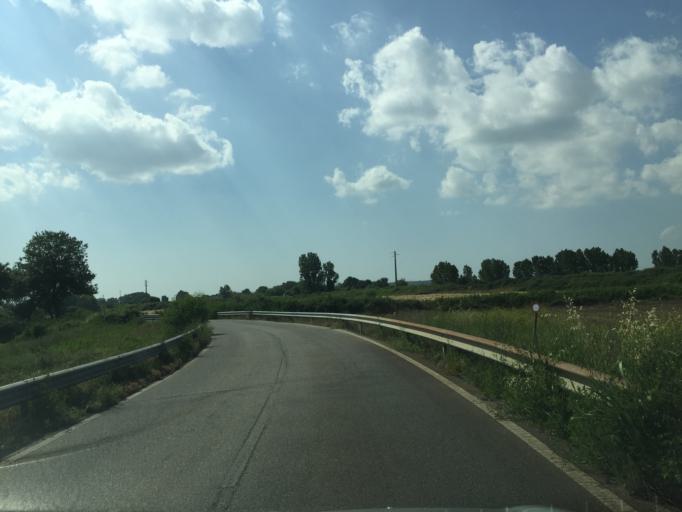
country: PT
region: Santarem
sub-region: Alpiarca
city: Alpiarca
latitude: 39.3021
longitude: -8.5605
